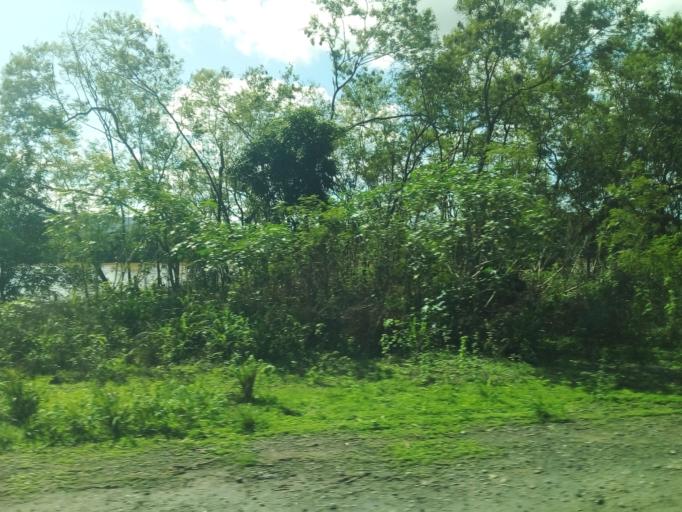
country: BR
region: Minas Gerais
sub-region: Governador Valadares
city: Governador Valadares
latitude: -18.8700
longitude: -41.7766
